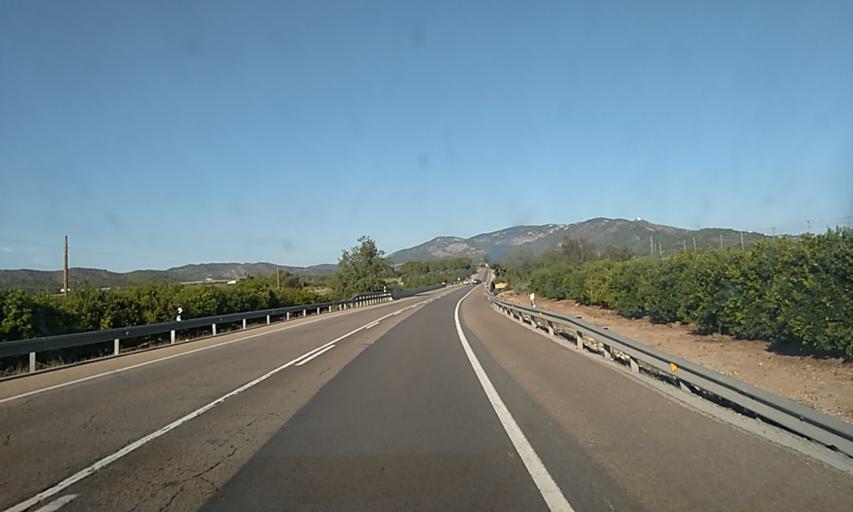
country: ES
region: Valencia
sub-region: Provincia de Castello
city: Torreblanca
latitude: 40.2385
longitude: 0.2249
